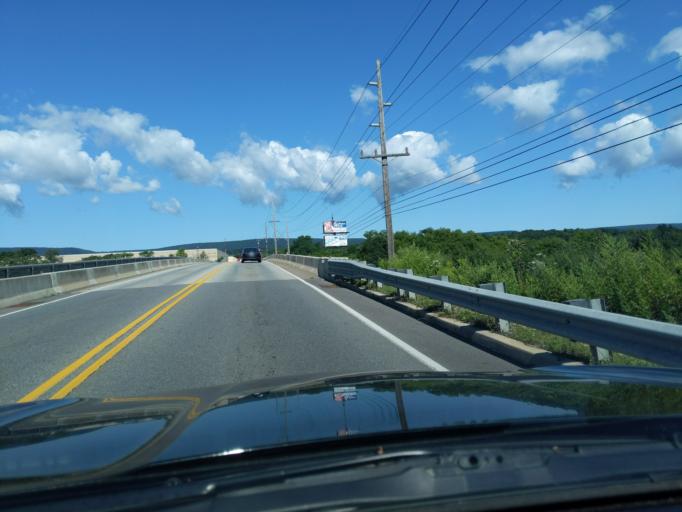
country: US
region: Pennsylvania
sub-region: Blair County
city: Greenwood
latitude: 40.5371
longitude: -78.3751
